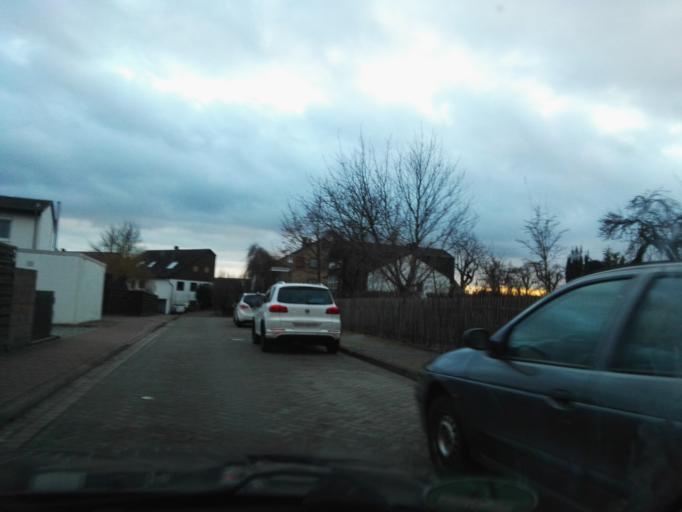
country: DE
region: Lower Saxony
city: Leiferde
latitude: 52.2087
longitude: 10.4655
